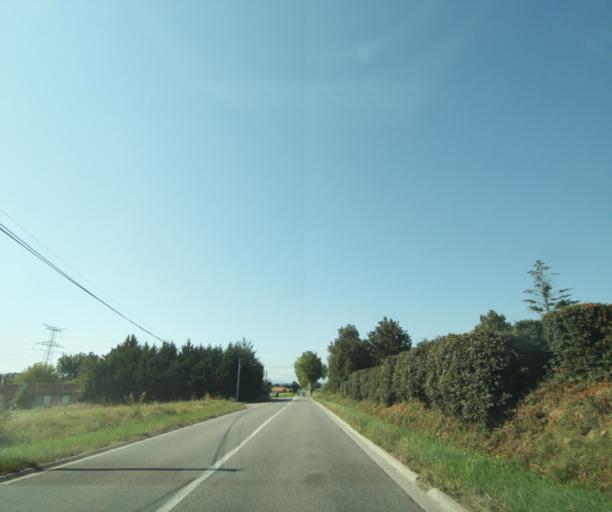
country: FR
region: Midi-Pyrenees
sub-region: Departement de la Haute-Garonne
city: Saint-Sulpice-sur-Leze
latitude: 43.3634
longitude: 1.3293
